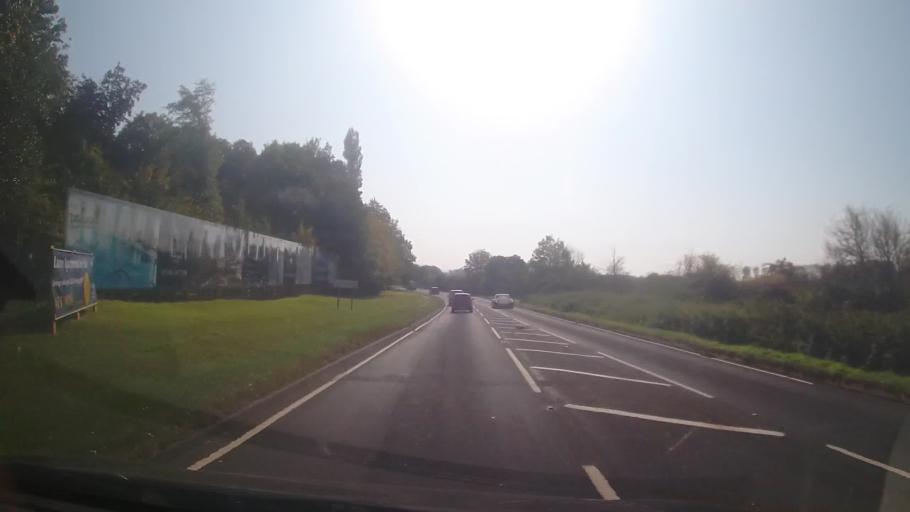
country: GB
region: England
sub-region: Worcestershire
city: Evesham
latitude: 52.1200
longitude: -1.9761
